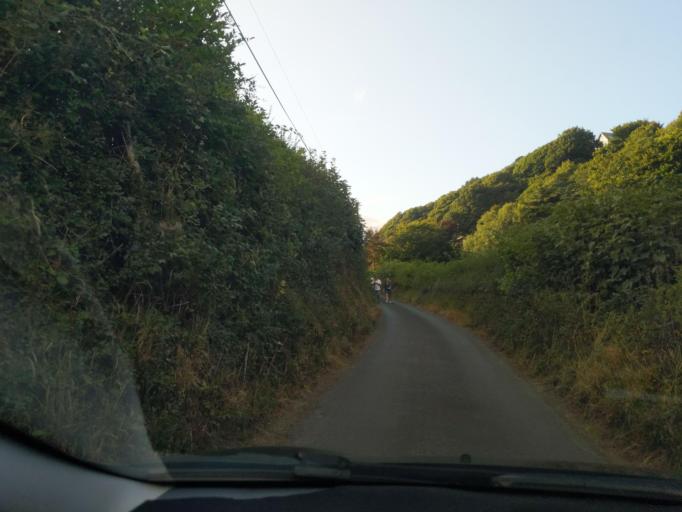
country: GB
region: England
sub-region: Devon
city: Salcombe
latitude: 50.2267
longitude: -3.7904
